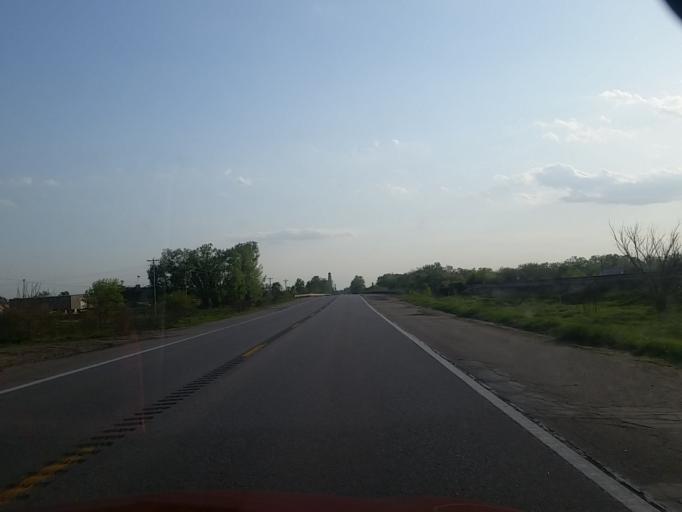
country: US
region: Nebraska
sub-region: Saunders County
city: Ashland
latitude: 41.0694
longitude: -96.3127
